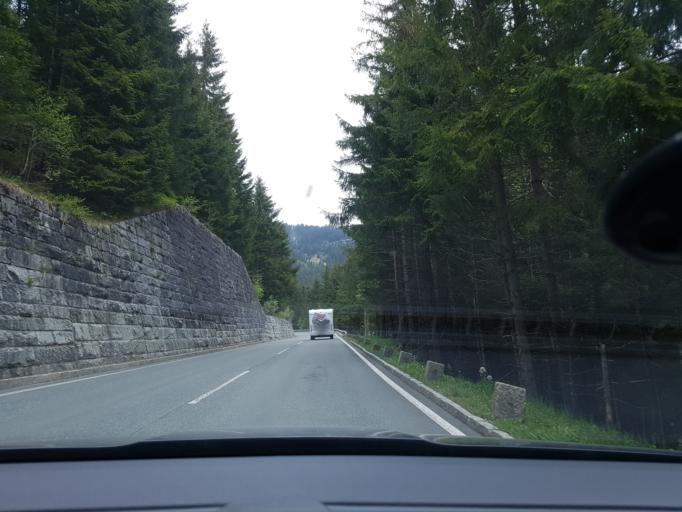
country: AT
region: Salzburg
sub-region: Politischer Bezirk Zell am See
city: Krimml
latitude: 47.2170
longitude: 12.1624
